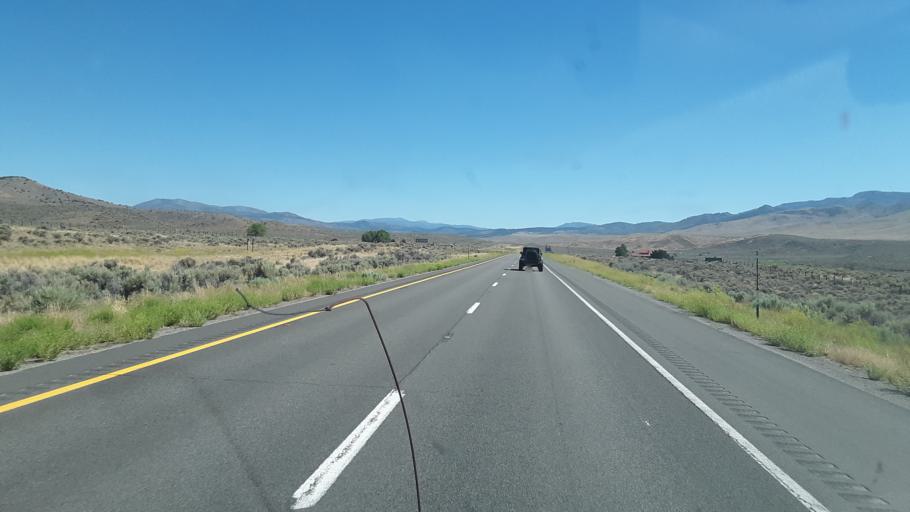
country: US
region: Nevada
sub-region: Washoe County
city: Cold Springs
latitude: 39.7371
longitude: -120.0394
